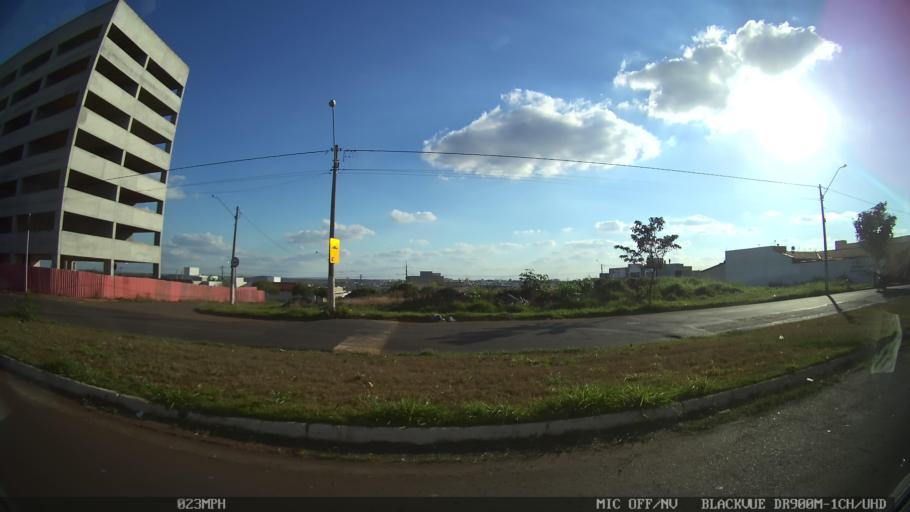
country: BR
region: Sao Paulo
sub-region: Santa Barbara D'Oeste
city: Santa Barbara d'Oeste
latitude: -22.7521
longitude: -47.3979
